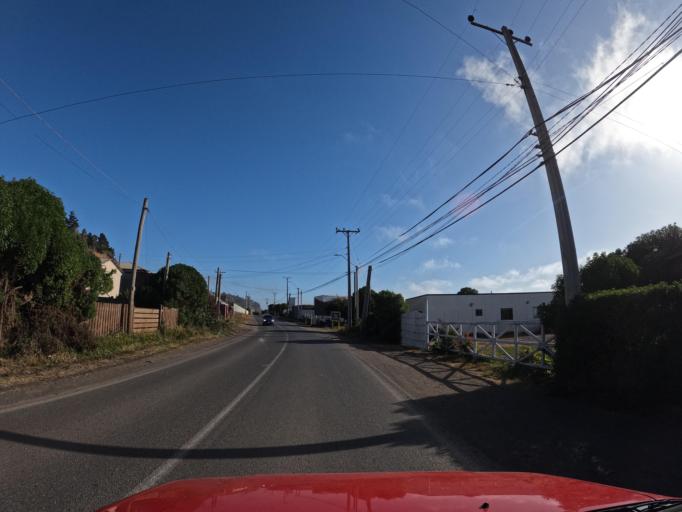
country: CL
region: Maule
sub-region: Provincia de Talca
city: Constitucion
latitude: -34.8960
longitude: -72.1791
